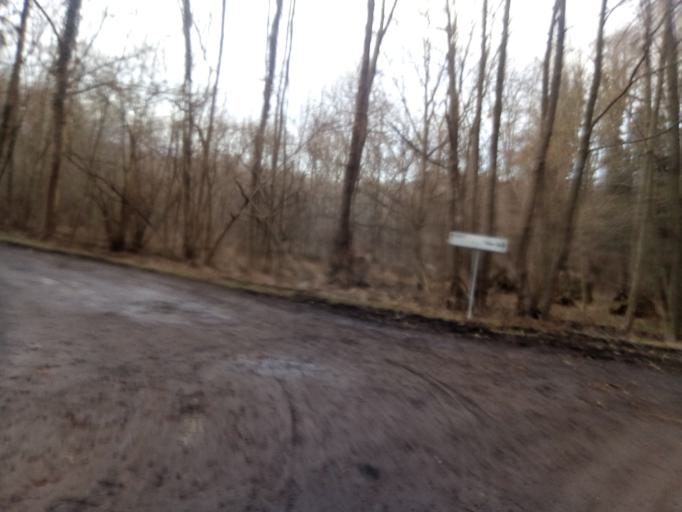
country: IT
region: Piedmont
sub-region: Provincia di Torino
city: Burolo
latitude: 45.4910
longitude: 7.9206
